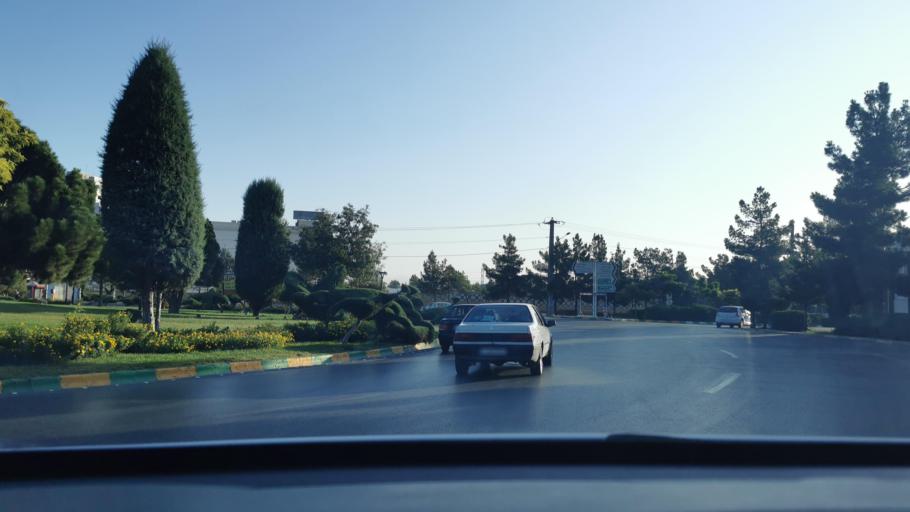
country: IR
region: Razavi Khorasan
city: Mashhad
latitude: 36.3589
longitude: 59.5131
